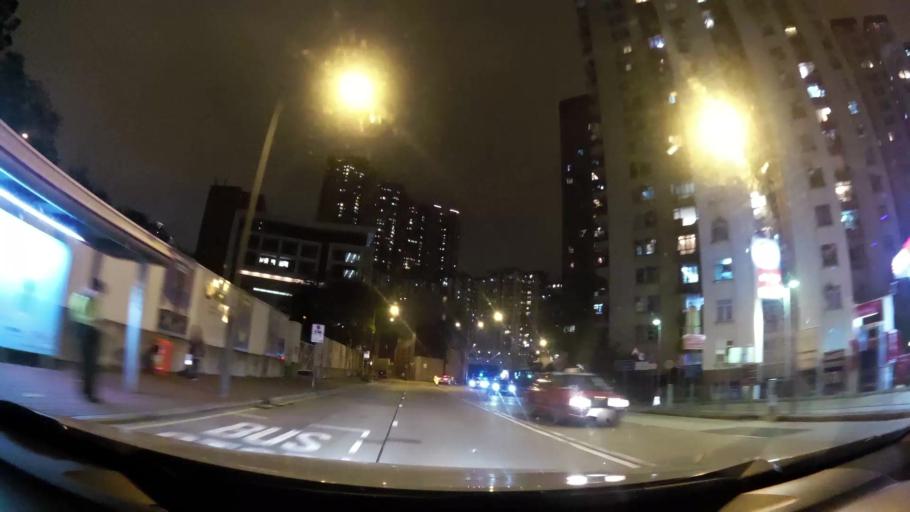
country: HK
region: Sham Shui Po
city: Sham Shui Po
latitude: 22.3383
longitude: 114.1407
